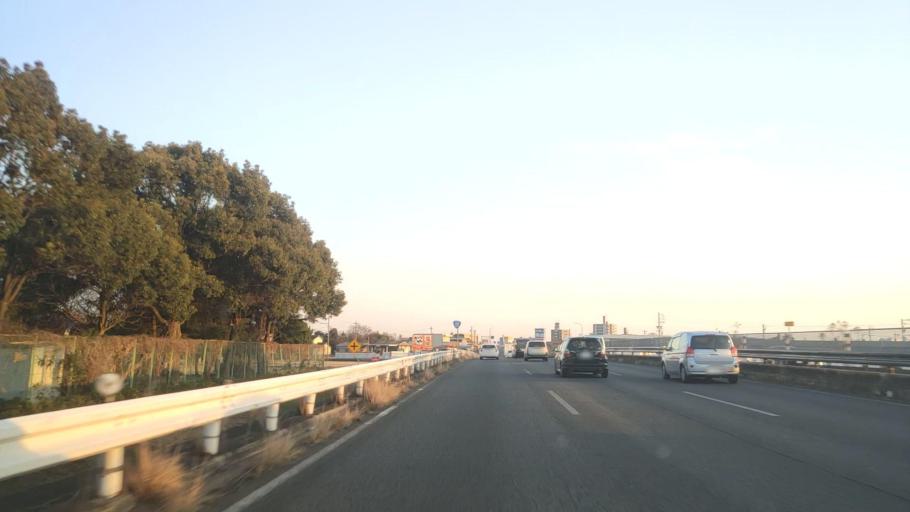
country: JP
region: Aichi
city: Kuroda
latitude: 35.3304
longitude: 136.8040
